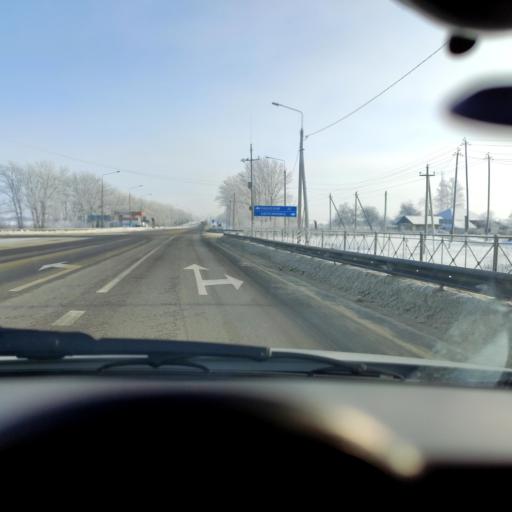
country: RU
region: Belgorod
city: Troitskiy
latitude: 51.6181
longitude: 37.5327
